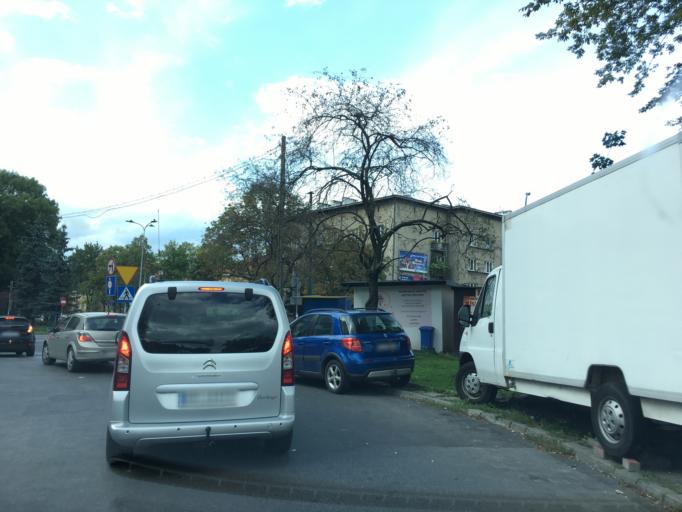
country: PL
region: Lesser Poland Voivodeship
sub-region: Krakow
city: Krakow
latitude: 50.0743
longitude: 19.9362
